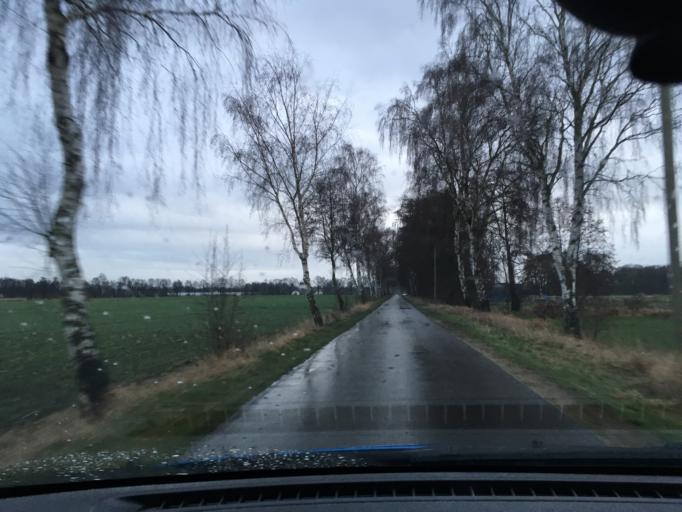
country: DE
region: Lower Saxony
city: Ludersburg
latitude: 53.3166
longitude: 10.6025
